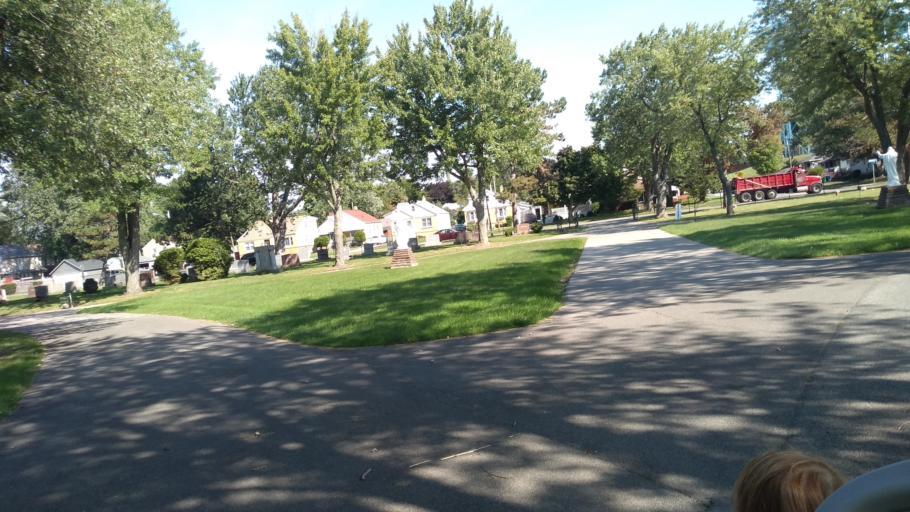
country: US
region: New York
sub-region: Erie County
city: Lackawanna
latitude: 42.8312
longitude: -78.8129
